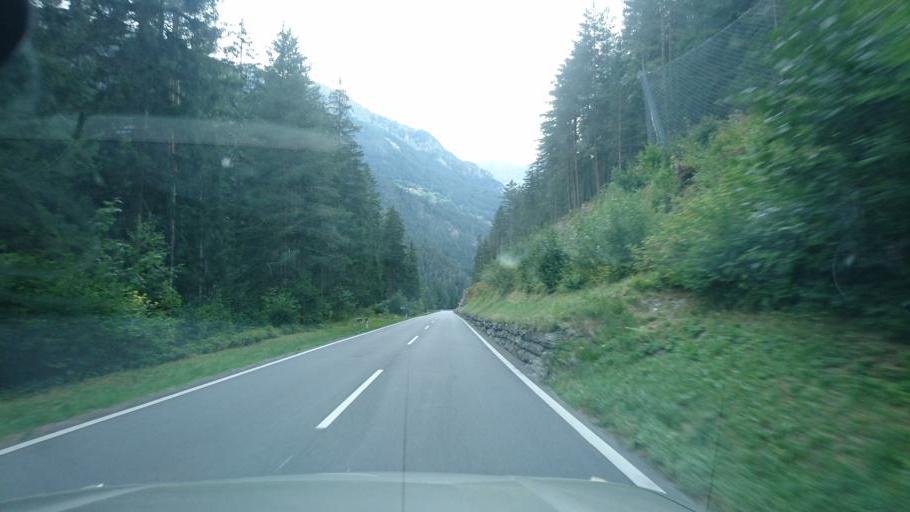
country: AT
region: Tyrol
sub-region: Politischer Bezirk Landeck
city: Pfunds
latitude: 46.9449
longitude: 10.5080
